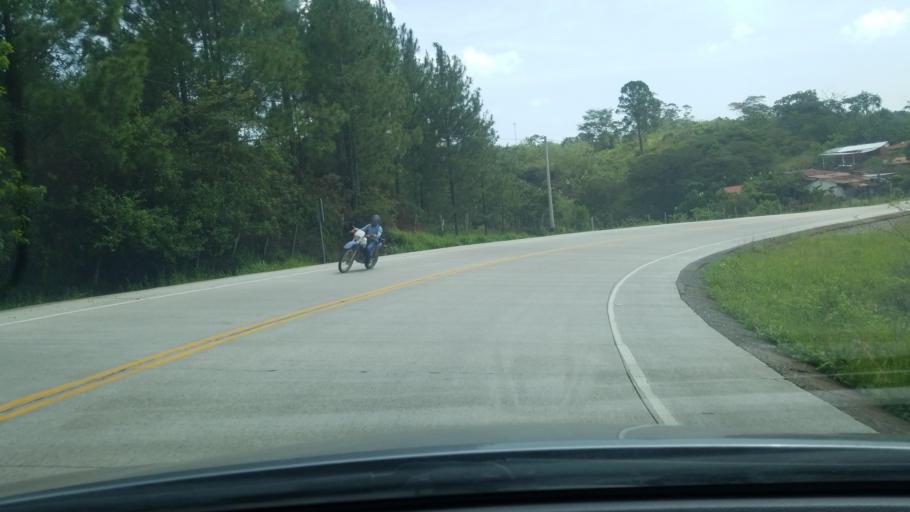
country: HN
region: Copan
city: San Jeronimo
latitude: 14.9394
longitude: -88.9178
